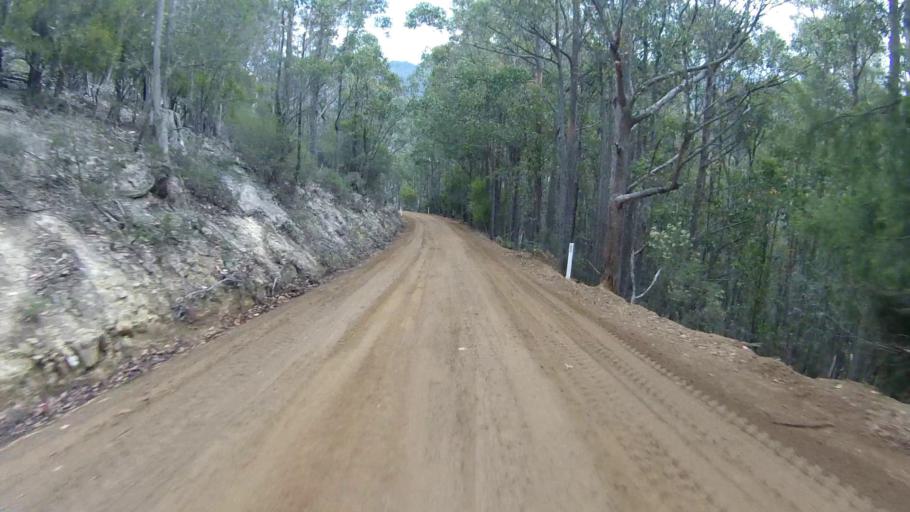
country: AU
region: Tasmania
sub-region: Huon Valley
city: Huonville
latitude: -42.9651
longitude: 147.0480
